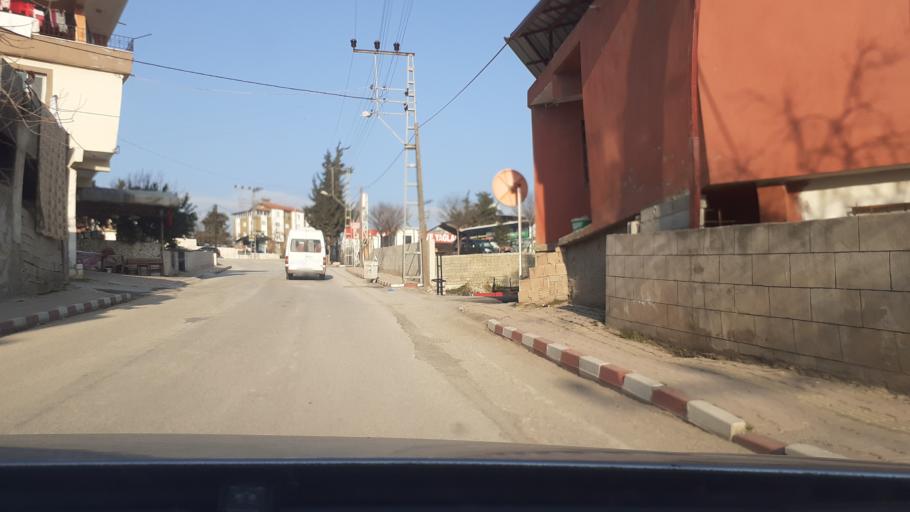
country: TR
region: Hatay
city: Fatikli
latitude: 36.1136
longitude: 36.2631
